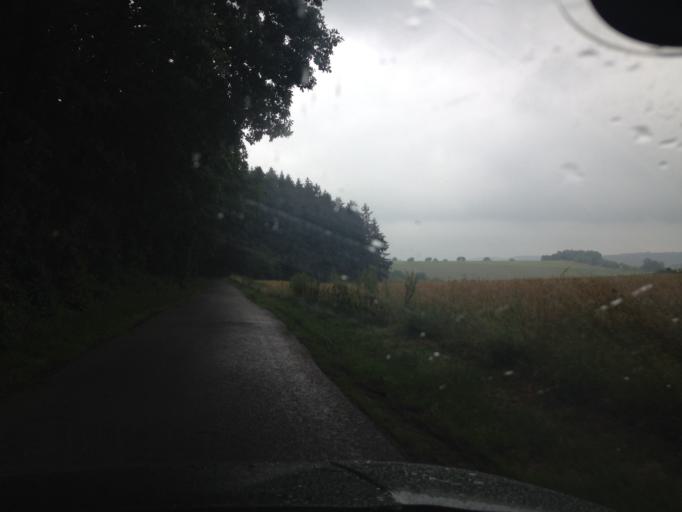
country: DE
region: Saarland
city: Marpingen
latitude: 49.4442
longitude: 7.0928
